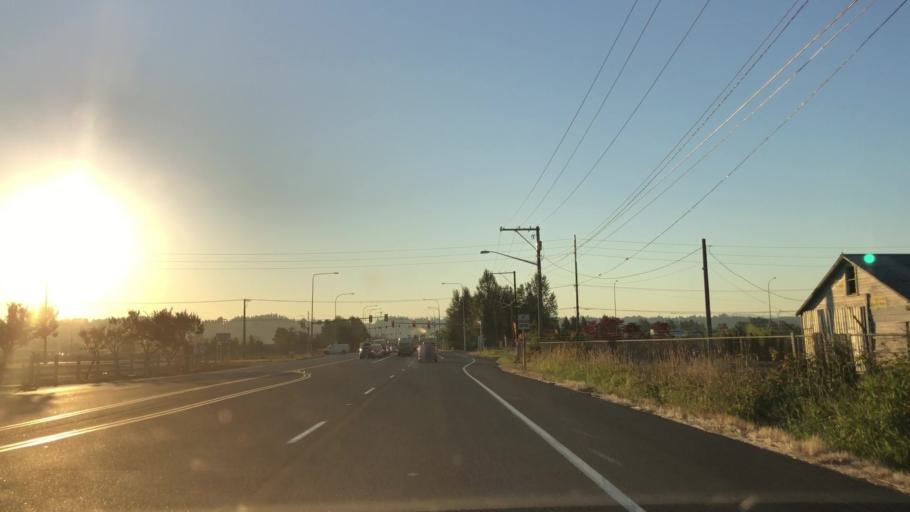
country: US
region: Washington
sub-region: King County
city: Kent
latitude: 47.3537
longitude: -122.2517
